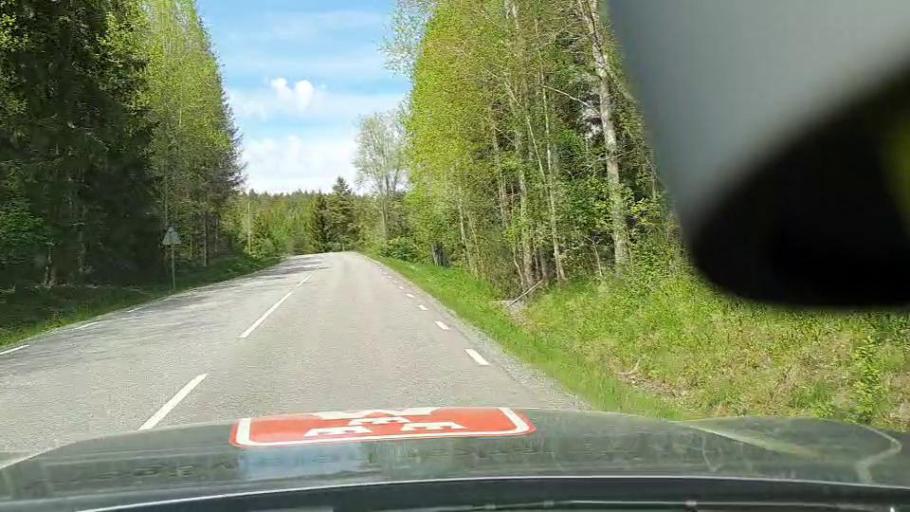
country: SE
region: Soedermanland
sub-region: Eskilstuna Kommun
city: Skogstorp
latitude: 59.2533
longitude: 16.4758
